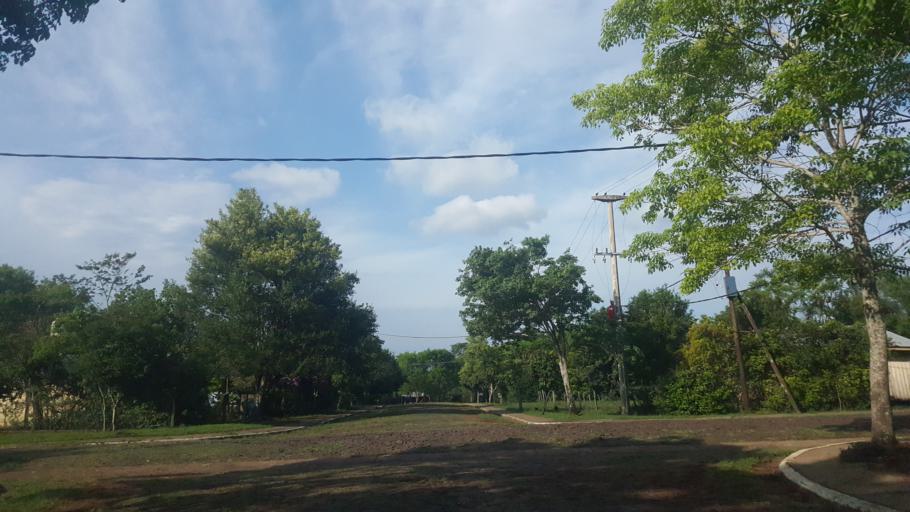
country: AR
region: Misiones
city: Cerro Cora
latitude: -27.5603
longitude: -55.7056
